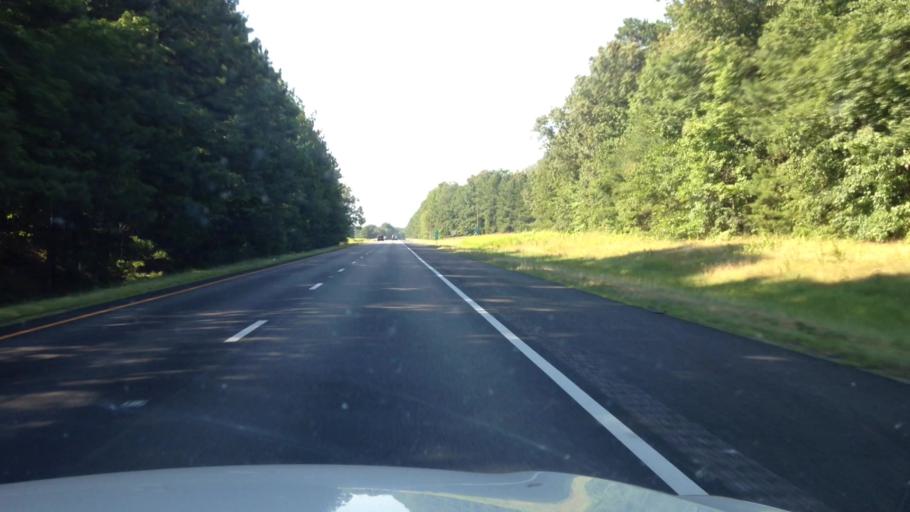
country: US
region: Virginia
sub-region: Sussex County
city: Sussex
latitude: 37.0164
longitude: -77.3917
